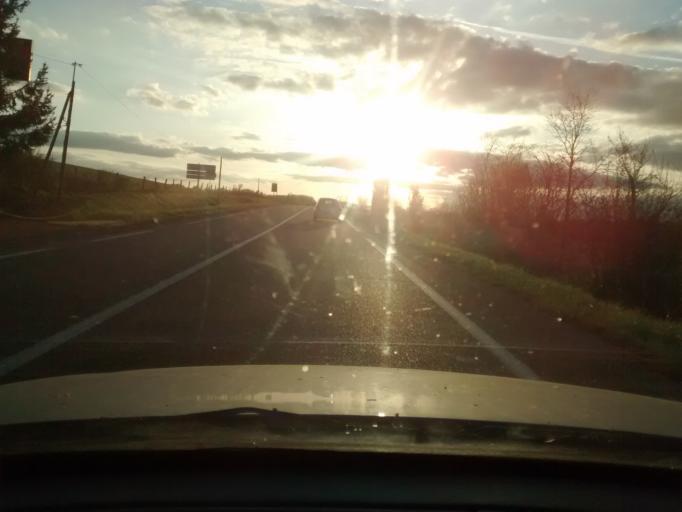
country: FR
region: Pays de la Loire
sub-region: Departement de la Mayenne
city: Sainte-Suzanne
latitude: 48.0377
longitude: -0.3926
